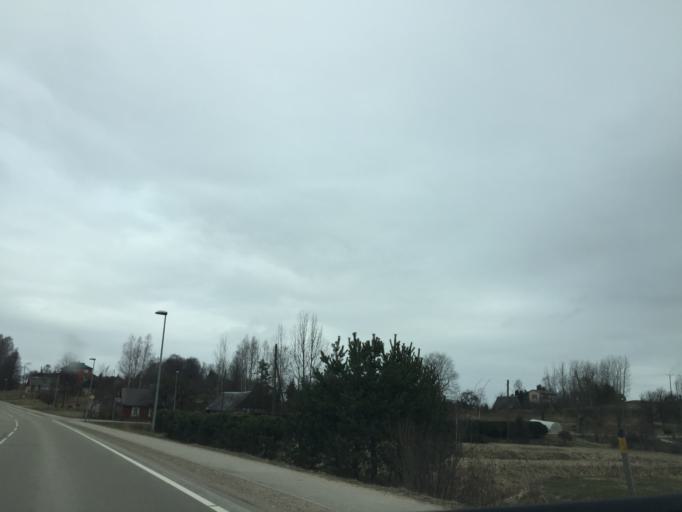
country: LV
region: Kraslavas Rajons
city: Kraslava
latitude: 55.9091
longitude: 27.1549
